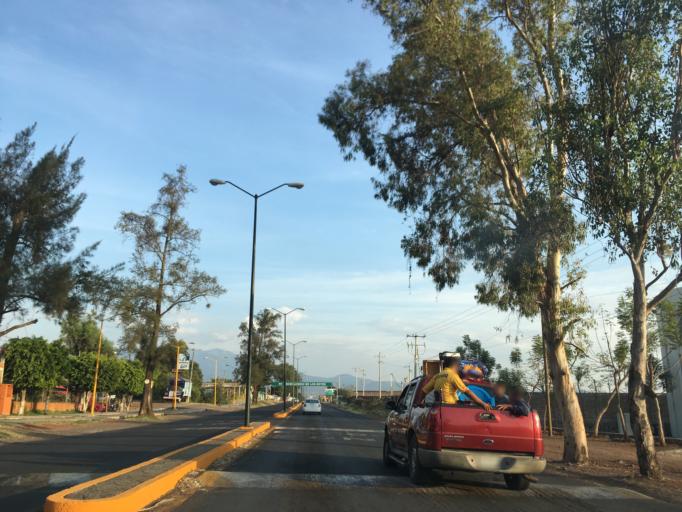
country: MX
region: Michoacan
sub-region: Los Reyes
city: La Higuerita (Colonia San Rafael)
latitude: 19.6150
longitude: -102.4835
